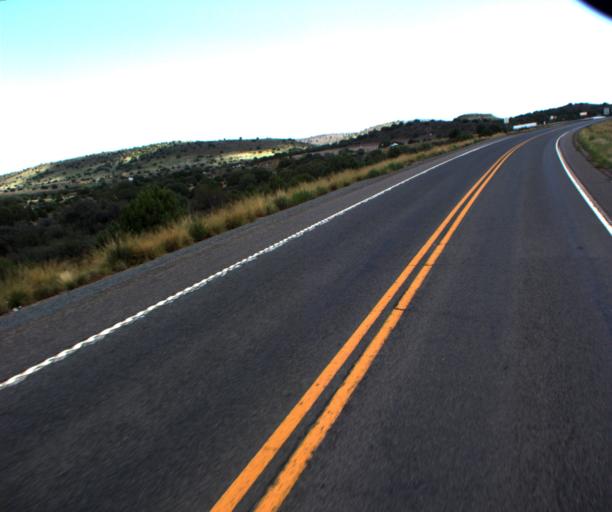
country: US
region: Arizona
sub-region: Yavapai County
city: Camp Verde
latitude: 34.5148
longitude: -111.9961
